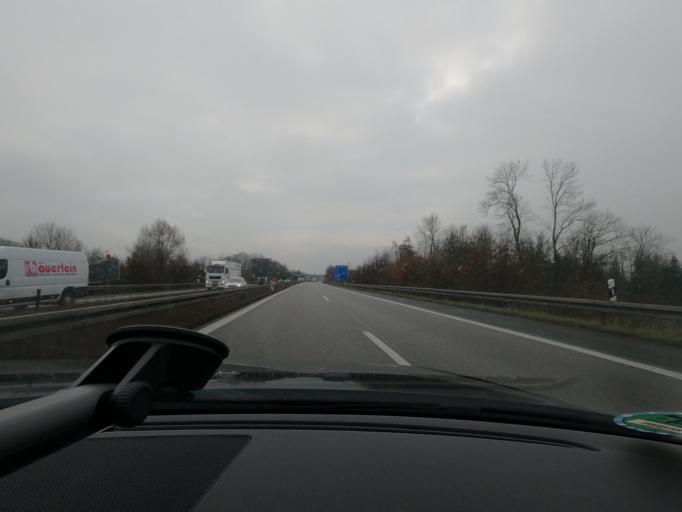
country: DE
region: Bavaria
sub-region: Upper Franconia
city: Hirschaid
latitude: 49.8328
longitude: 11.0063
